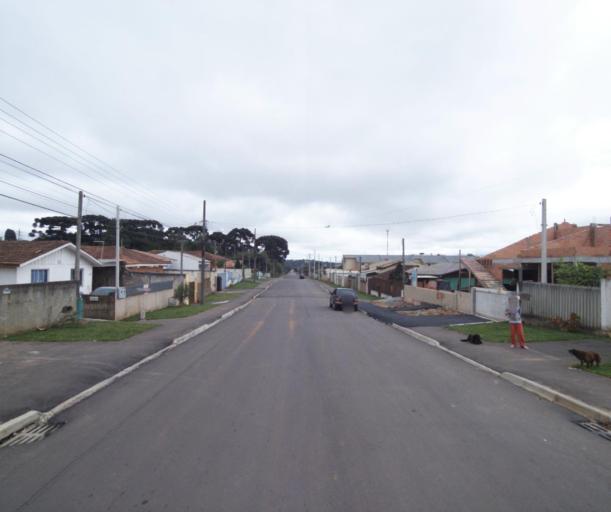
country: BR
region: Parana
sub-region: Quatro Barras
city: Quatro Barras
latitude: -25.3640
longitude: -49.1106
